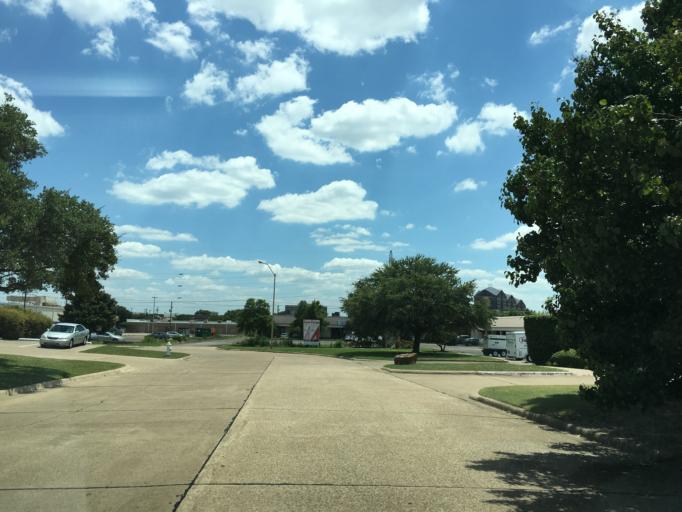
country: US
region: Texas
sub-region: Dallas County
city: Addison
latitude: 32.9487
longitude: -96.8368
